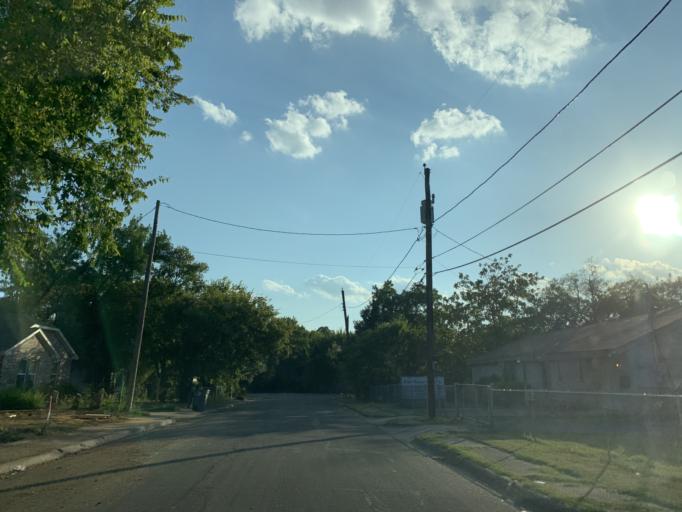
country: US
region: Texas
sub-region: Dallas County
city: Dallas
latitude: 32.7002
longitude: -96.7870
